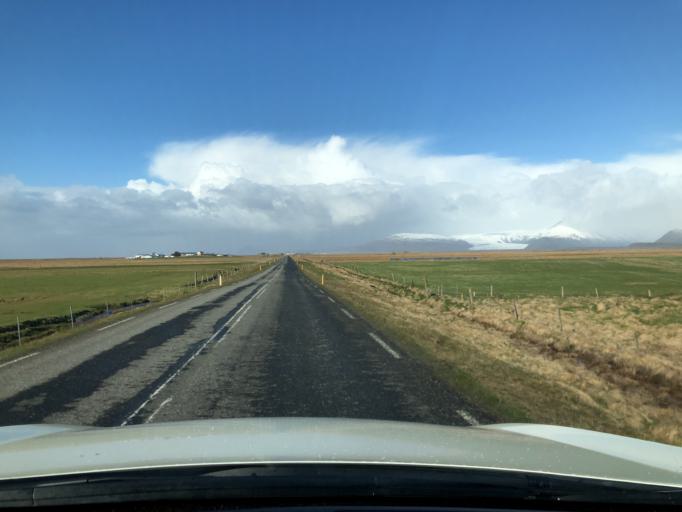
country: IS
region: East
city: Hoefn
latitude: 64.2989
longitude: -15.4221
